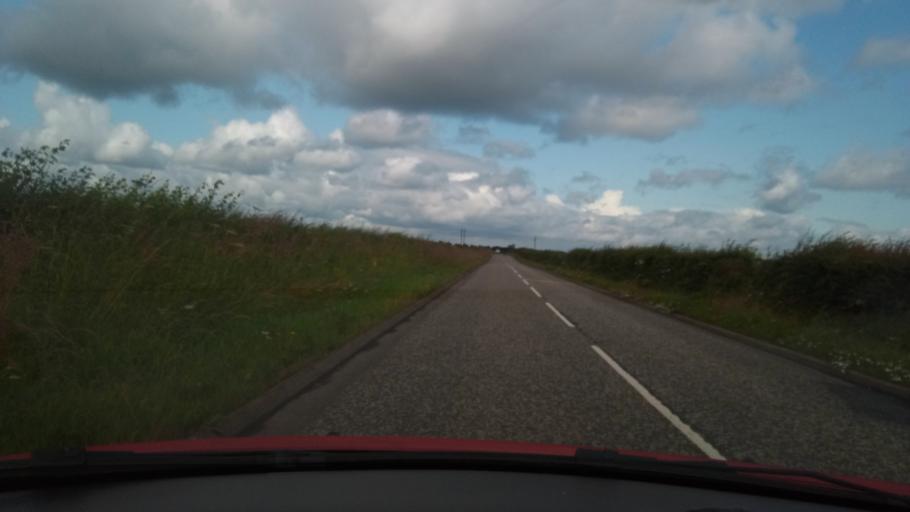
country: GB
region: Scotland
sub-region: East Lothian
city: Macmerry
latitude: 55.9316
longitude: -2.9262
